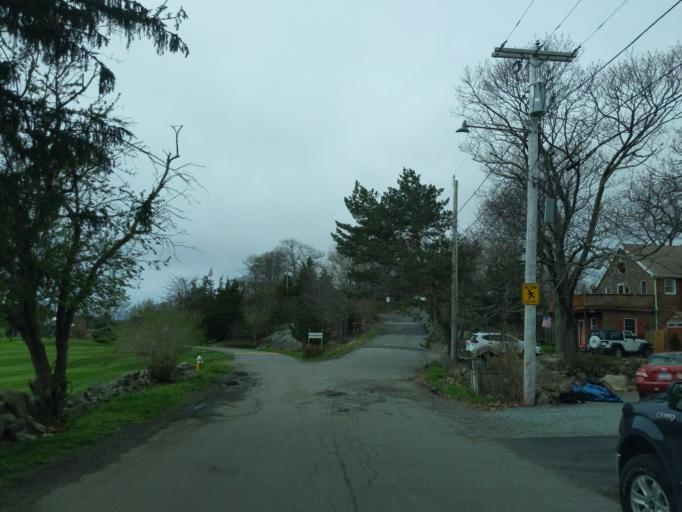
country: US
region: Massachusetts
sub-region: Essex County
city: Rockport
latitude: 42.6517
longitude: -70.6059
